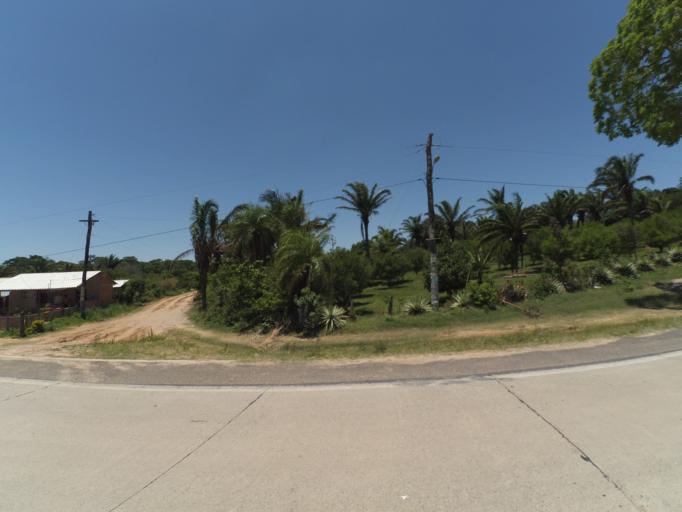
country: BO
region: Santa Cruz
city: Santa Cruz de la Sierra
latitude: -17.8232
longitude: -63.2901
